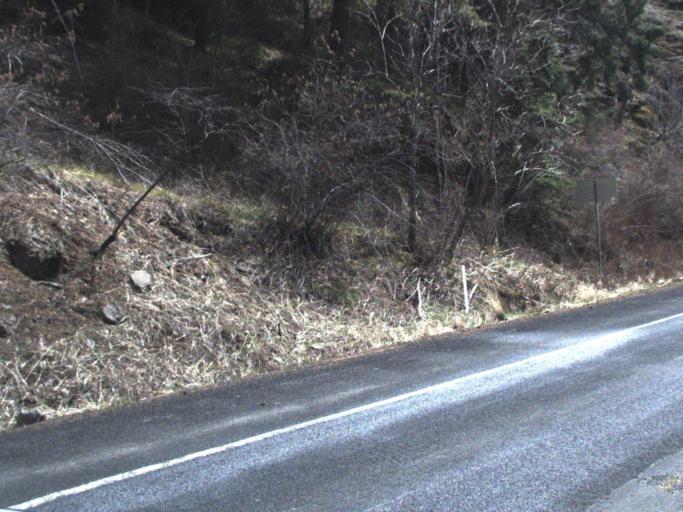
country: US
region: Washington
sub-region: Kittitas County
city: Cle Elum
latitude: 46.9382
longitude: -121.0605
